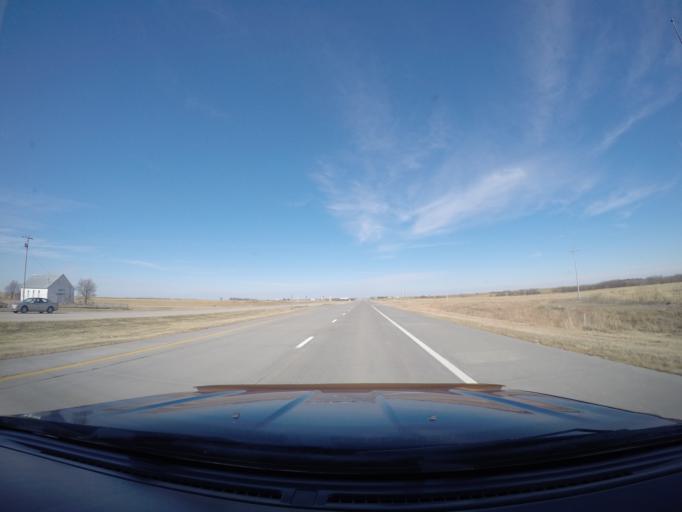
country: US
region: Kansas
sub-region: Republic County
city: Belleville
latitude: 39.9708
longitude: -97.6130
